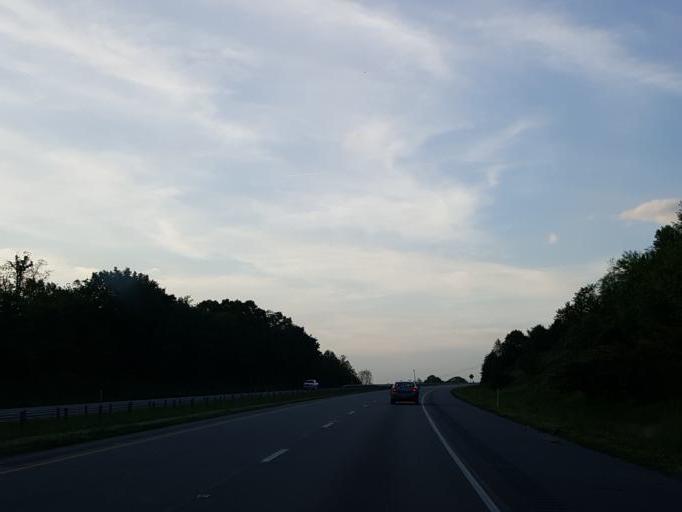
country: US
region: Pennsylvania
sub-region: Blair County
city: Duncansville
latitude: 40.4031
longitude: -78.4345
